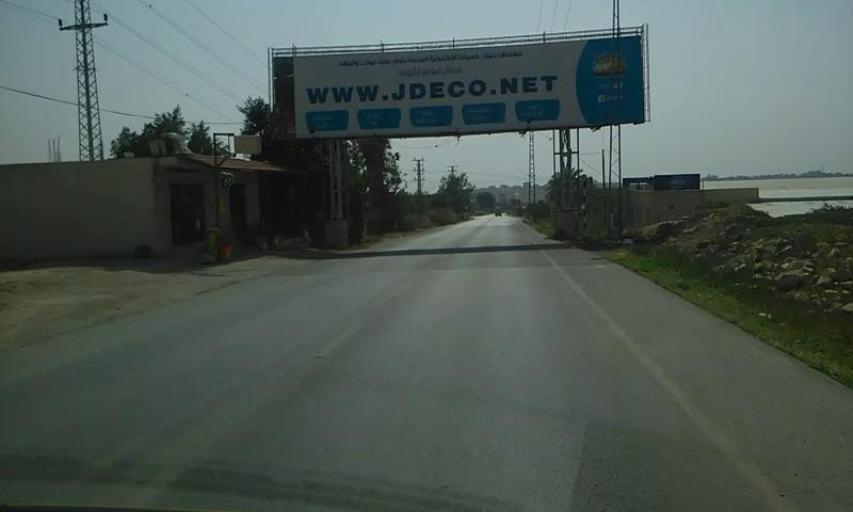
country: PS
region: West Bank
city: An Nuway`imah
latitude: 31.8893
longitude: 35.4329
